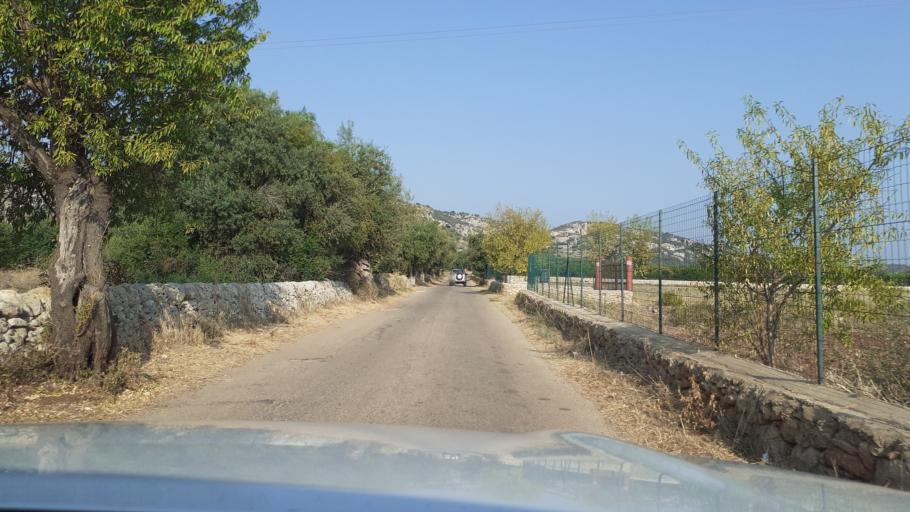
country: IT
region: Sicily
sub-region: Provincia di Siracusa
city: Cassibile
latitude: 36.9759
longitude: 15.1832
